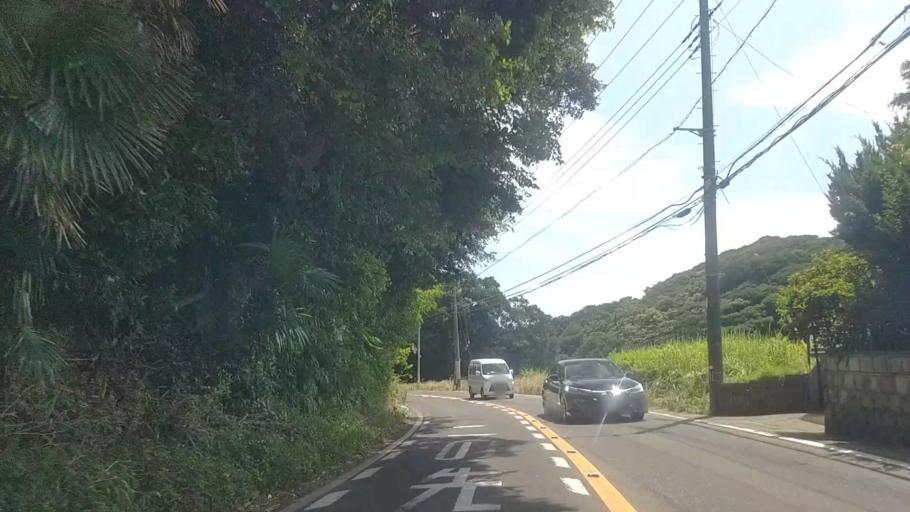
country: JP
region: Kanagawa
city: Miura
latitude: 35.2044
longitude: 139.6486
